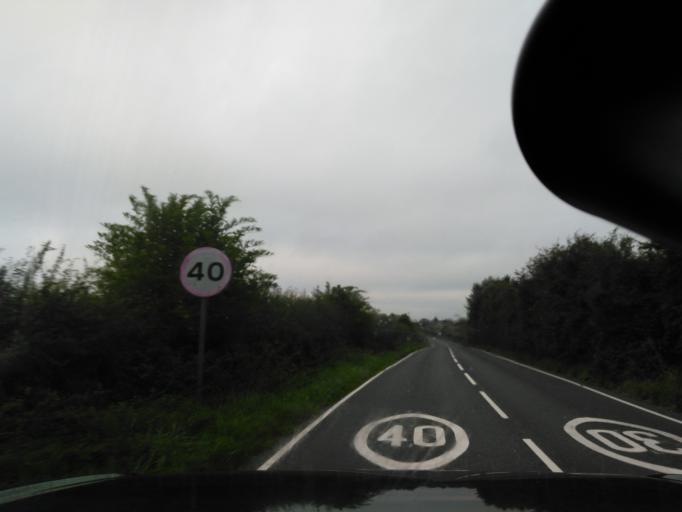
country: GB
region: England
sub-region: Dorset
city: Lytchett Matravers
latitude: 50.7947
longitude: -2.0800
